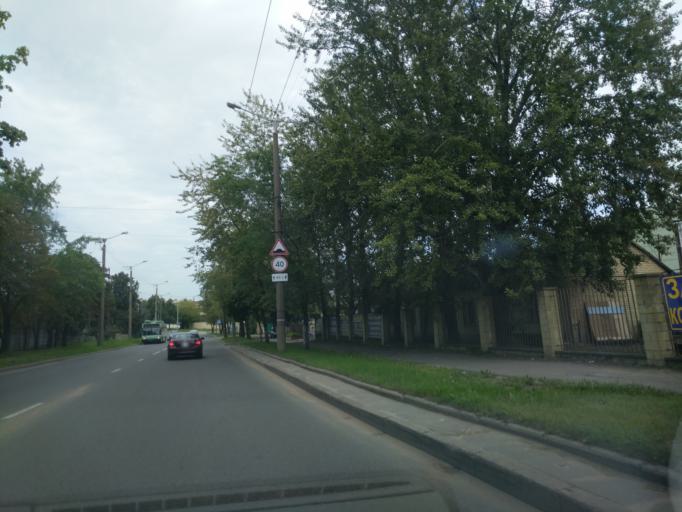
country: BY
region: Minsk
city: Novoye Medvezhino
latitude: 53.8902
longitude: 27.4816
